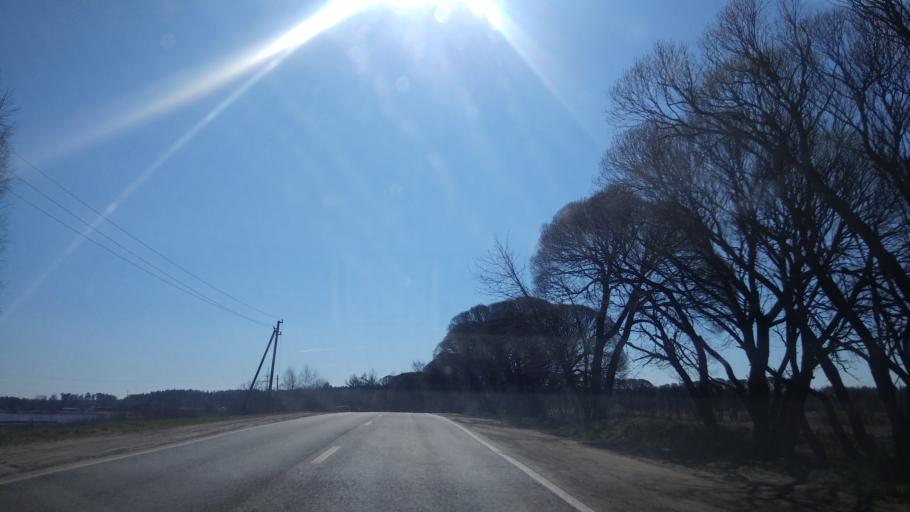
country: RU
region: Moskovskaya
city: Pravdinskiy
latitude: 56.0453
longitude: 37.8832
